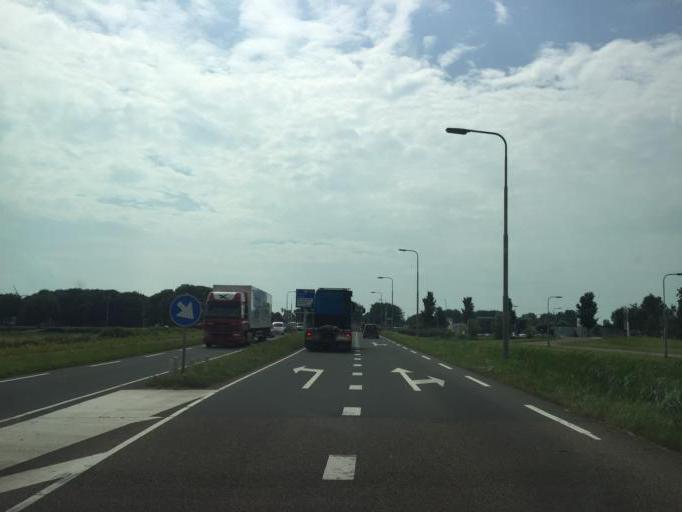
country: NL
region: North Holland
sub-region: Gemeente Enkhuizen
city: Enkhuizen
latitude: 52.6975
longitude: 5.2738
